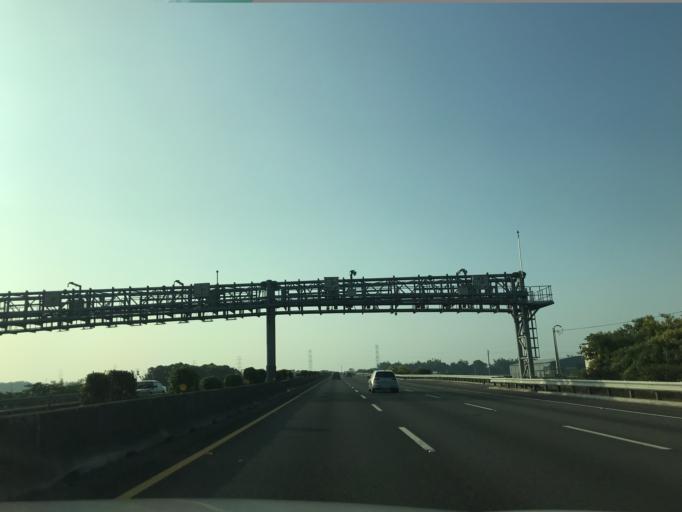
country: TW
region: Taiwan
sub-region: Yunlin
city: Douliu
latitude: 23.8312
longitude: 120.4848
